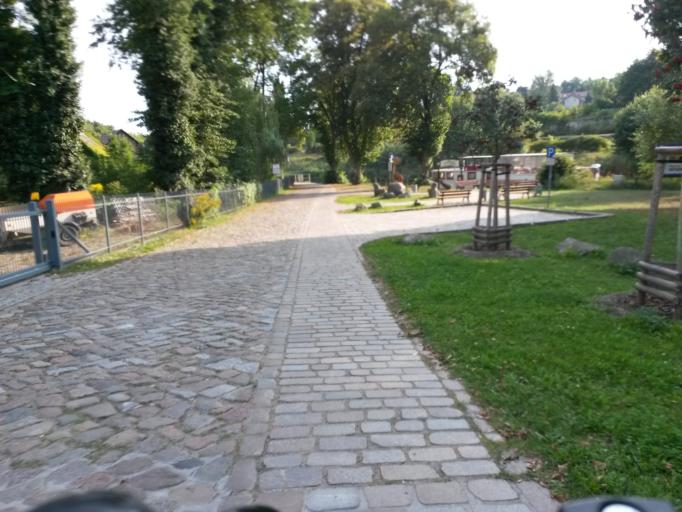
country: DE
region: Brandenburg
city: Templin
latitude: 53.1219
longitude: 13.4949
